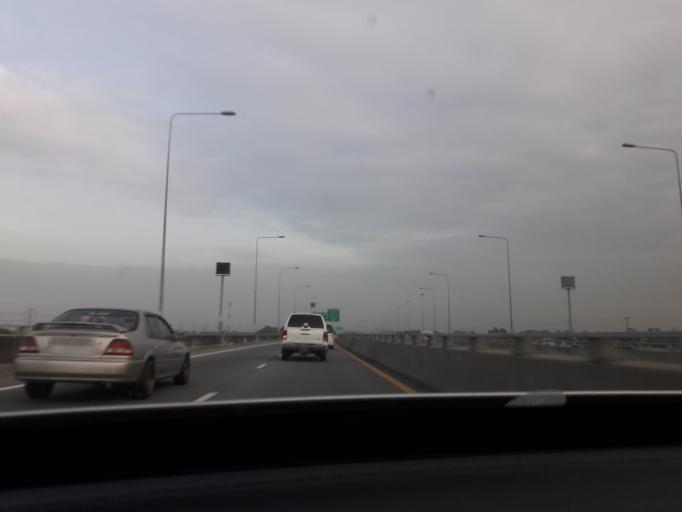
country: TH
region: Phra Nakhon Si Ayutthaya
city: Ban Bang Kadi Pathum Thani
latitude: 13.9897
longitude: 100.5683
